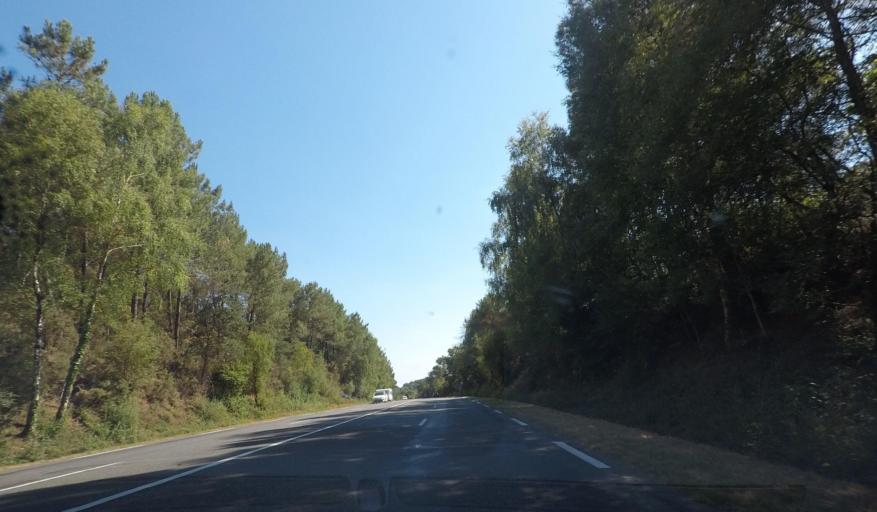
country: FR
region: Brittany
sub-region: Departement du Morbihan
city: Molac
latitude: 47.7086
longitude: -2.4444
